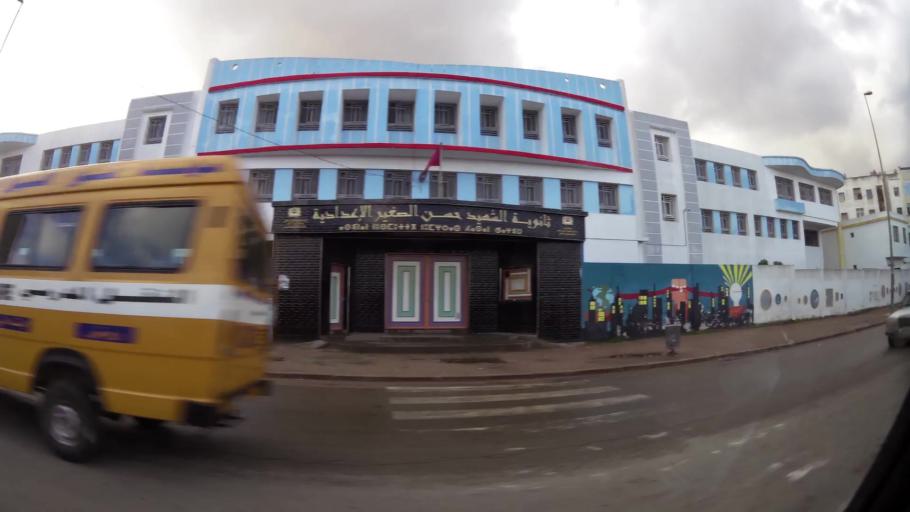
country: MA
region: Grand Casablanca
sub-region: Mediouna
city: Tit Mellil
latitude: 33.5846
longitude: -7.5283
